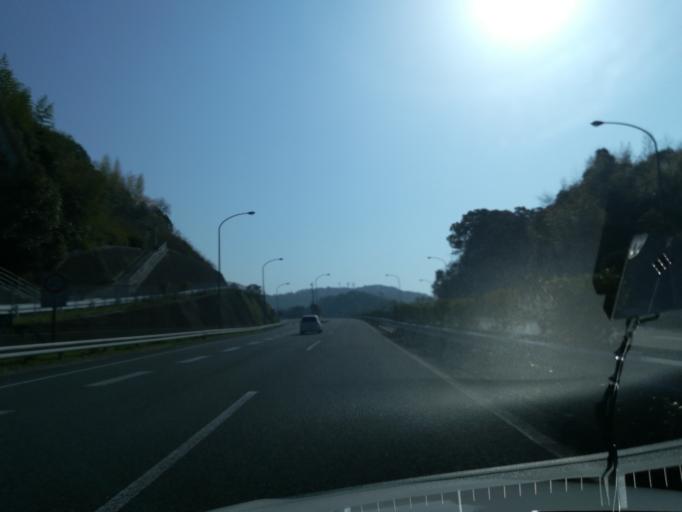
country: JP
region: Kochi
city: Kochi-shi
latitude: 33.6015
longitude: 133.6121
